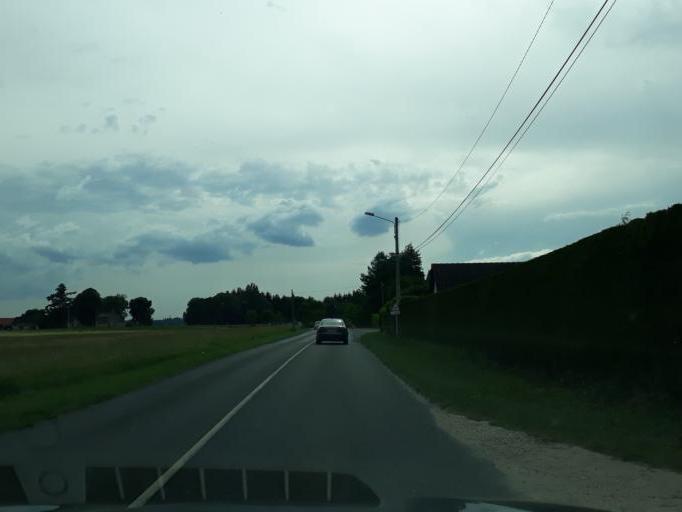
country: FR
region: Centre
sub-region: Departement du Loiret
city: Sandillon
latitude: 47.8429
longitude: 2.0177
